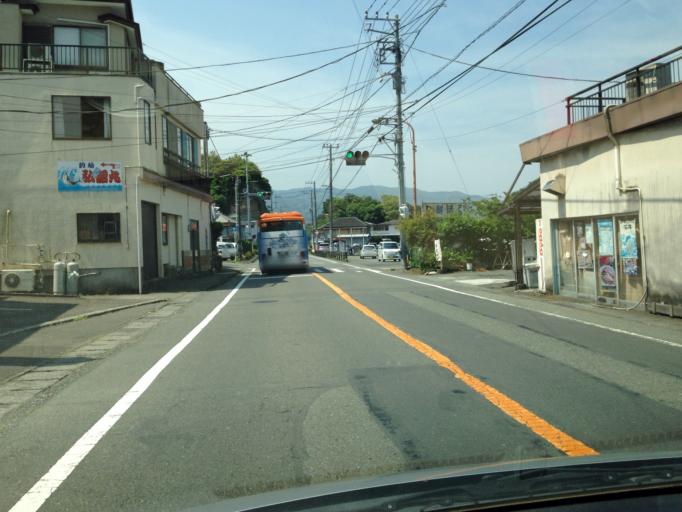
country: JP
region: Shizuoka
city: Numazu
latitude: 35.0338
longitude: 138.8951
